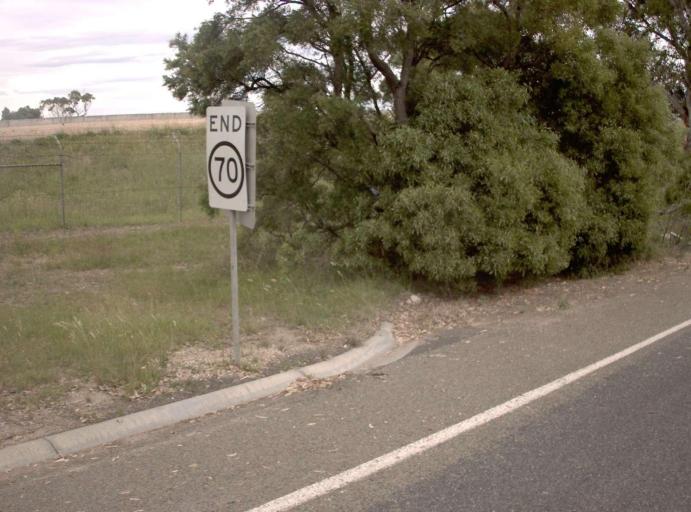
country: AU
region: Victoria
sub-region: East Gippsland
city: Bairnsdale
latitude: -37.7975
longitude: 147.6116
